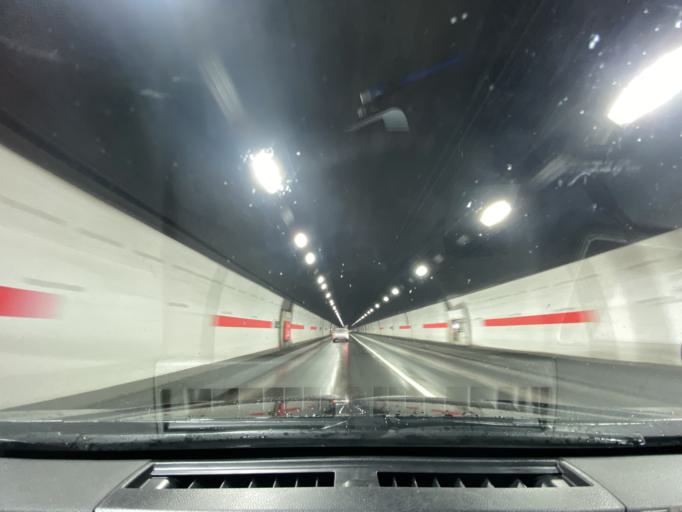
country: JP
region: Hokkaido
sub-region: Asahikawa-shi
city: Asahikawa
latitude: 43.7396
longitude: 142.2430
